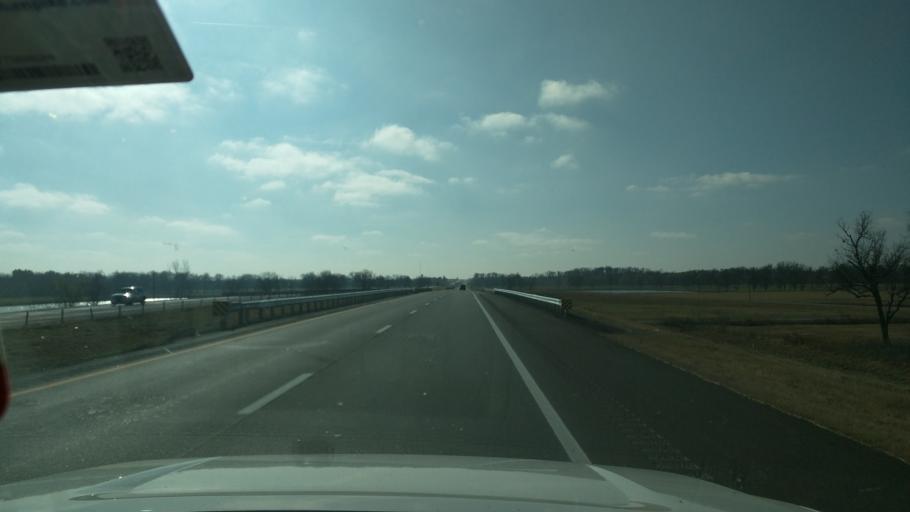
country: US
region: Oklahoma
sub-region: Washington County
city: Bartlesville
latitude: 36.6570
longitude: -95.9356
